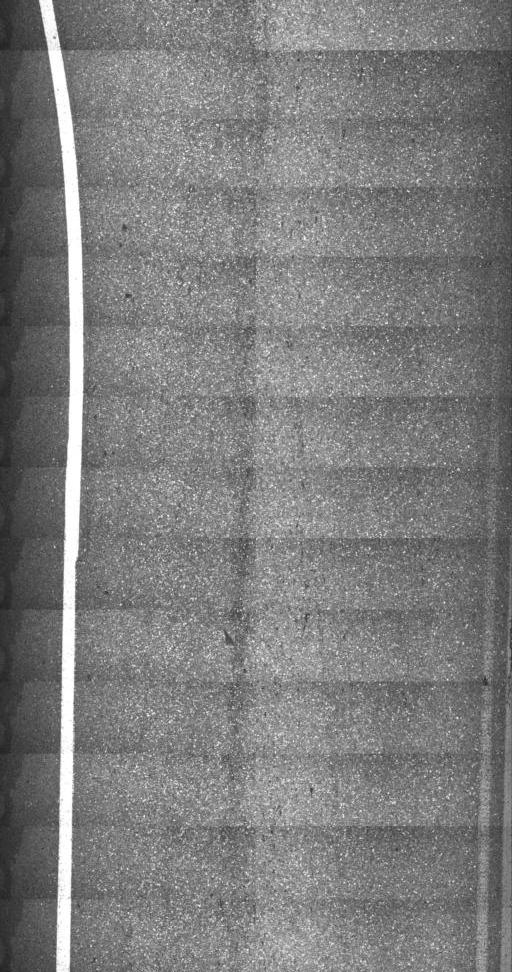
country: US
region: Vermont
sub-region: Lamoille County
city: Morristown
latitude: 44.5575
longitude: -72.6109
